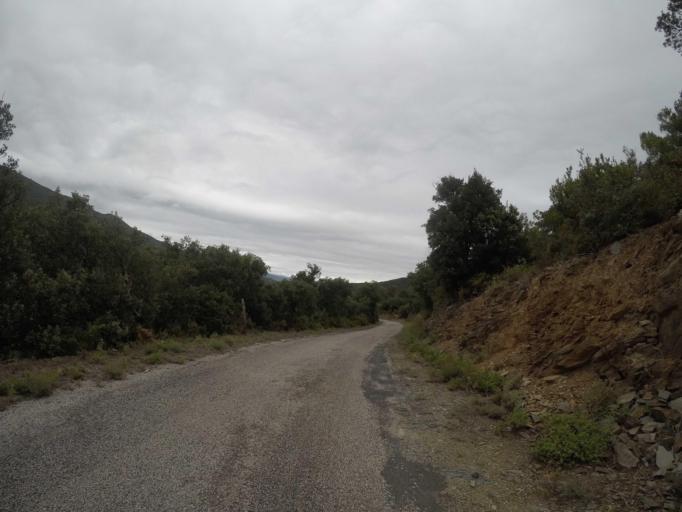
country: FR
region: Languedoc-Roussillon
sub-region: Departement des Pyrenees-Orientales
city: Ille-sur-Tet
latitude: 42.6133
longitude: 2.6073
